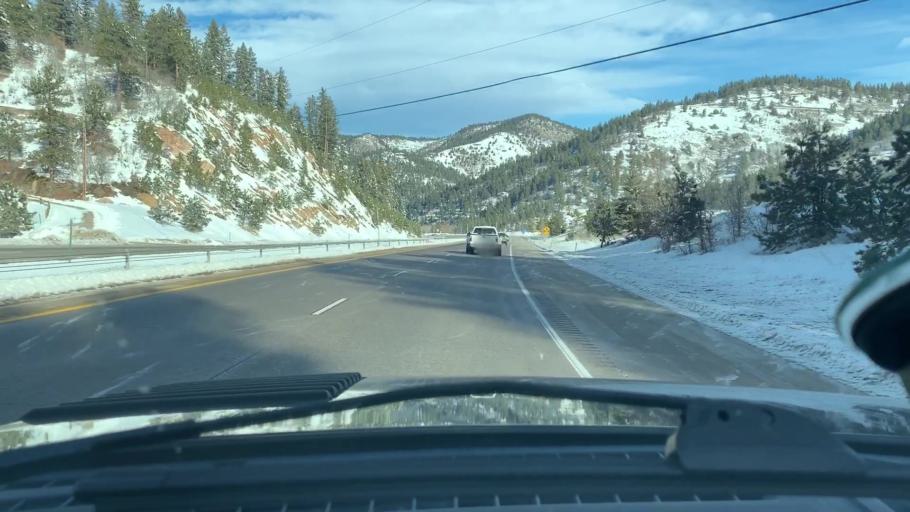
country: US
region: Colorado
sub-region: Jefferson County
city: Indian Hills
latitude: 39.6026
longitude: -105.2291
